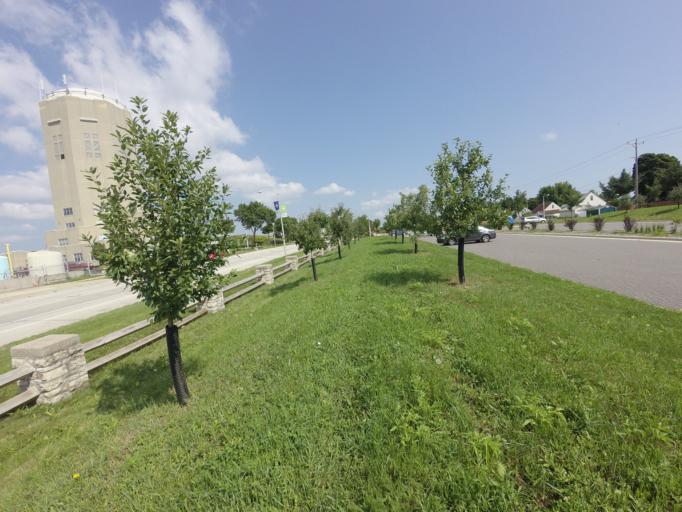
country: US
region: Wisconsin
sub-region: Milwaukee County
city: Saint Francis
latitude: 42.9714
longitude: -87.9192
